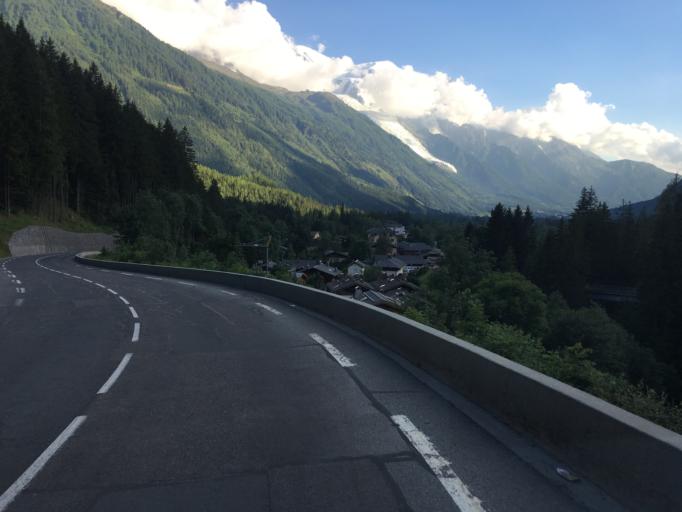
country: FR
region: Rhone-Alpes
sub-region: Departement de la Haute-Savoie
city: Chamonix-Mont-Blanc
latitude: 45.9566
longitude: 6.9028
